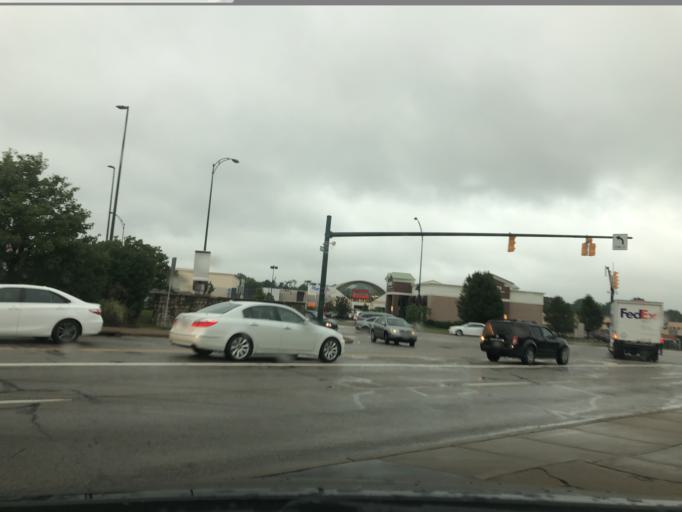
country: US
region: Ohio
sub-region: Hamilton County
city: Deer Park
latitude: 39.1995
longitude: -84.3805
